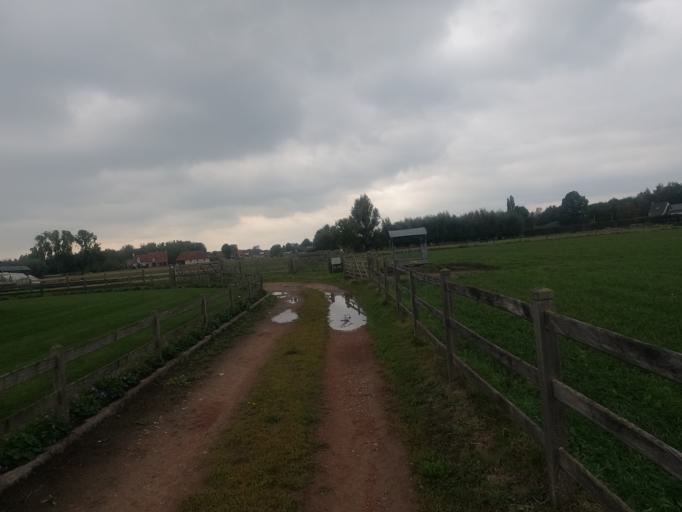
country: BE
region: Flanders
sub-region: Provincie Antwerpen
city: Berlaar
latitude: 51.0997
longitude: 4.6816
